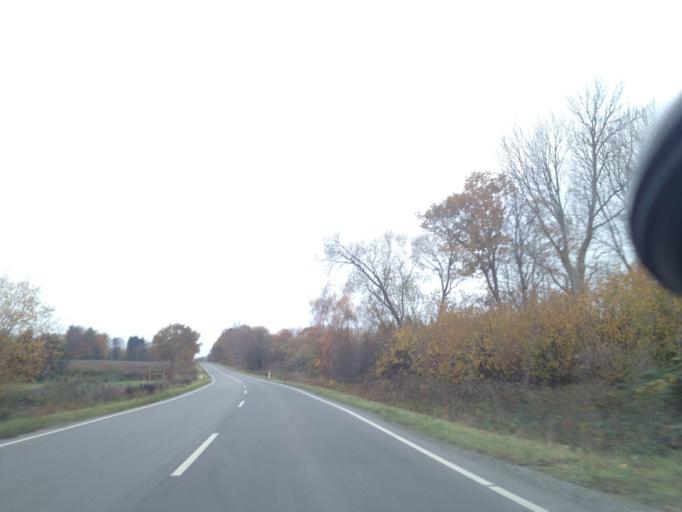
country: DK
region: South Denmark
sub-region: Nordfyns Kommune
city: Sonderso
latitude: 55.4311
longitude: 10.2450
